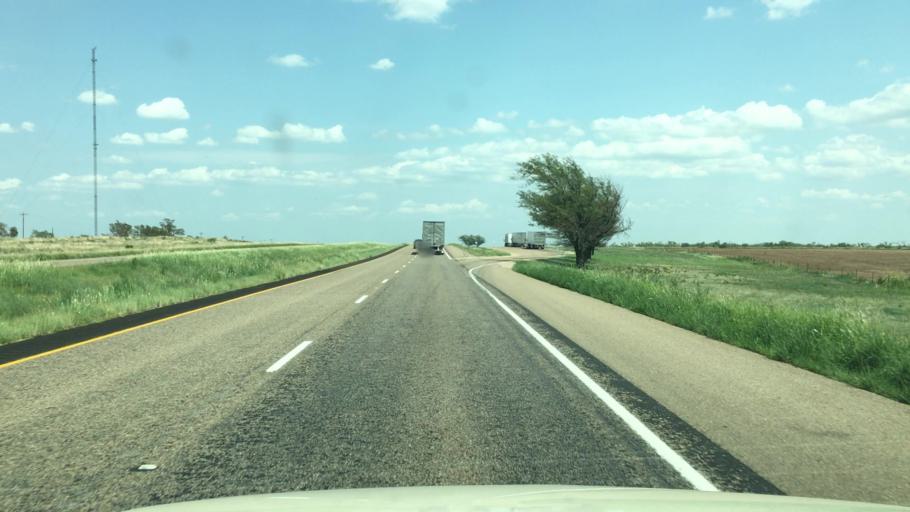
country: US
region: Texas
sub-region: Armstrong County
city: Claude
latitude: 35.0328
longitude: -101.1537
